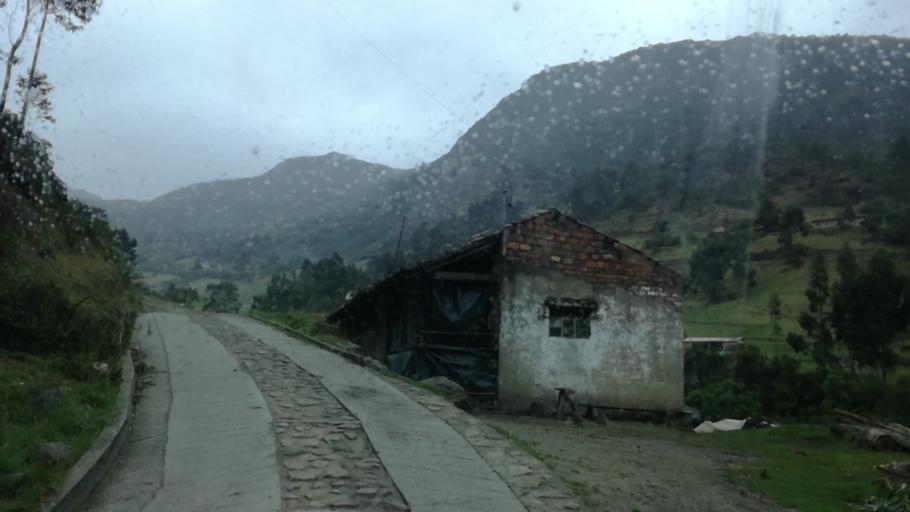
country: CO
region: Boyaca
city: Socha Viejo
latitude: 5.9338
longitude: -72.6914
